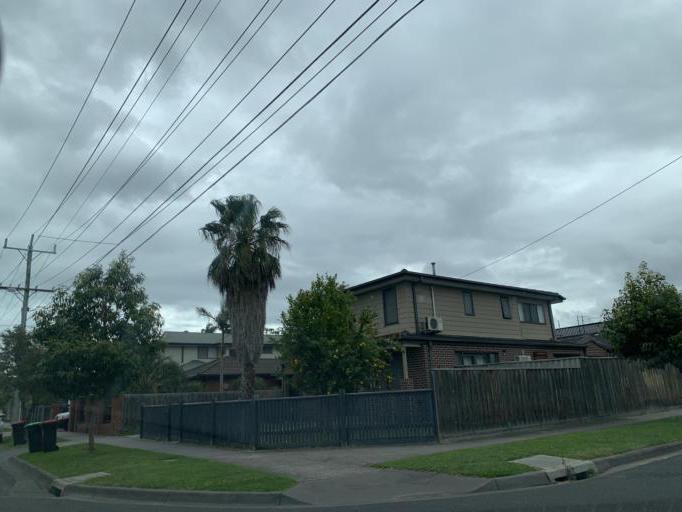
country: AU
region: Victoria
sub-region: Kingston
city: Mentone
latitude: -37.9698
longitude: 145.0724
